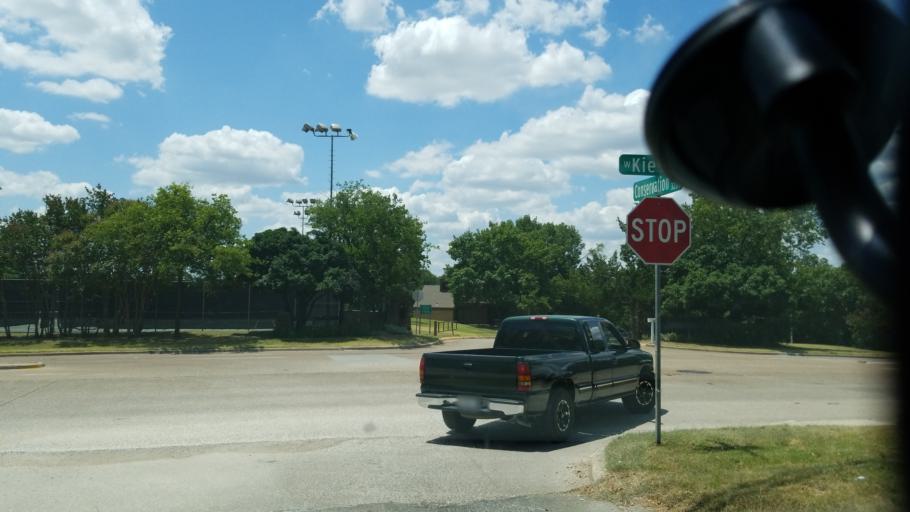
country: US
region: Texas
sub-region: Dallas County
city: Cockrell Hill
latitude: 32.7060
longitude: -96.8544
